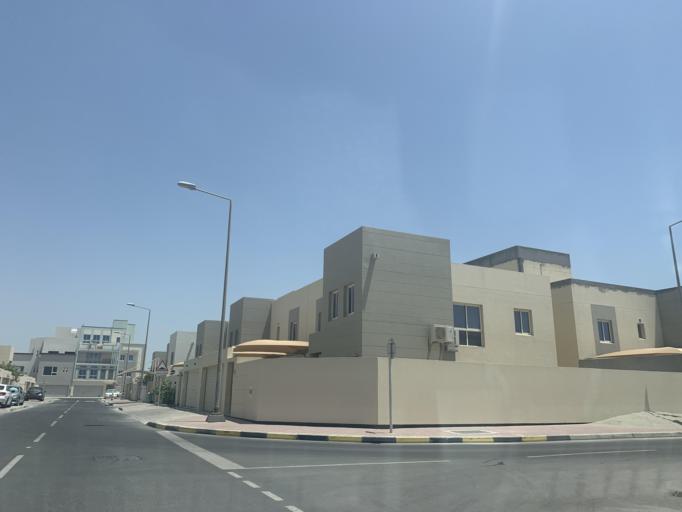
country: BH
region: Manama
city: Jidd Hafs
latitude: 26.2374
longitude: 50.4710
